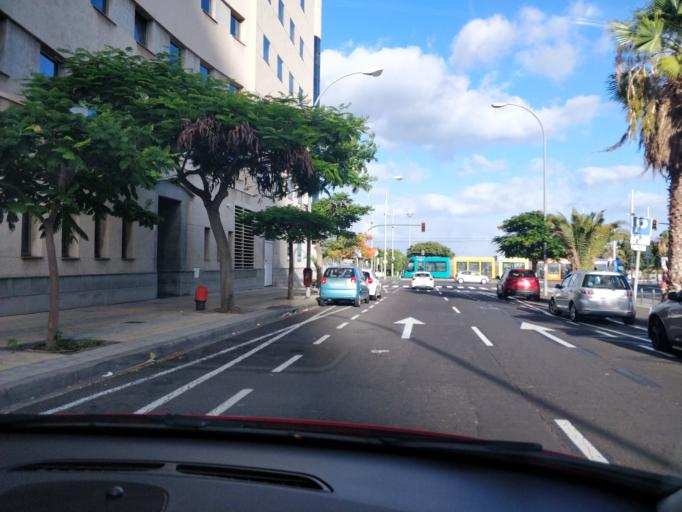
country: ES
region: Canary Islands
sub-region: Provincia de Santa Cruz de Tenerife
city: Santa Cruz de Tenerife
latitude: 28.4598
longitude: -16.2516
